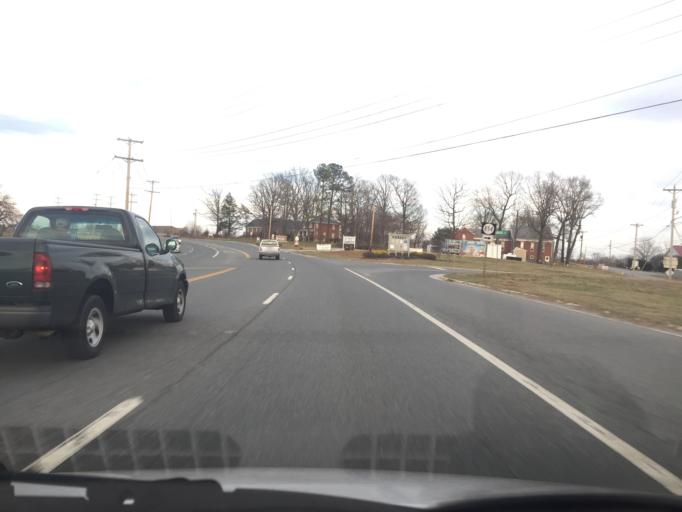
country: US
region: Virginia
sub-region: Bedford County
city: Forest
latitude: 37.3641
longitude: -79.2909
